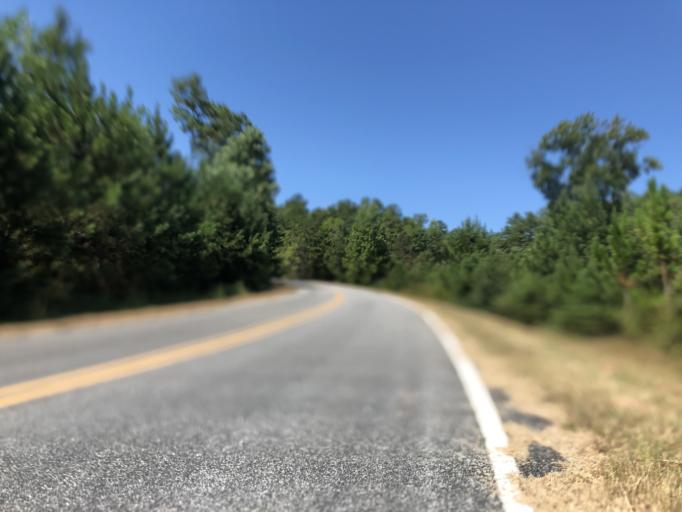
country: US
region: Georgia
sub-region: Heard County
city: Franklin
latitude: 33.3886
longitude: -84.9993
